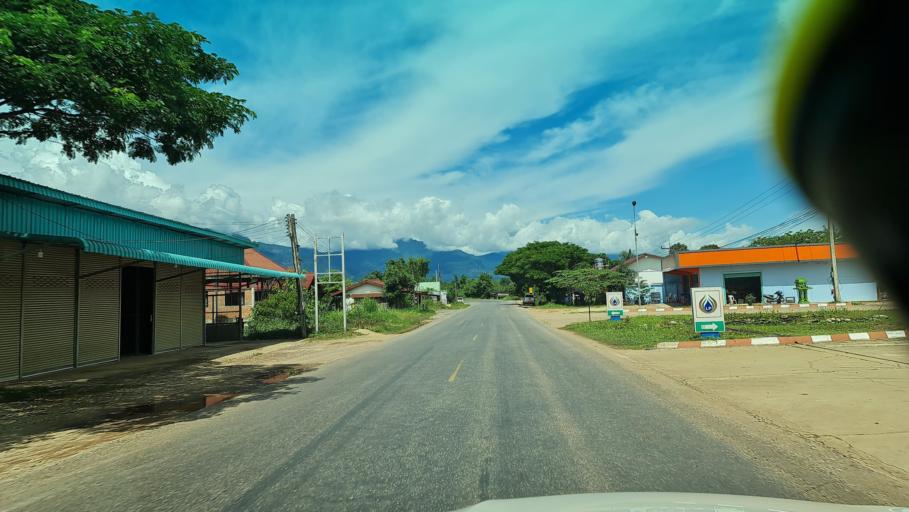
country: LA
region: Bolikhamxai
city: Pakkading
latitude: 18.2991
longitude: 104.1043
